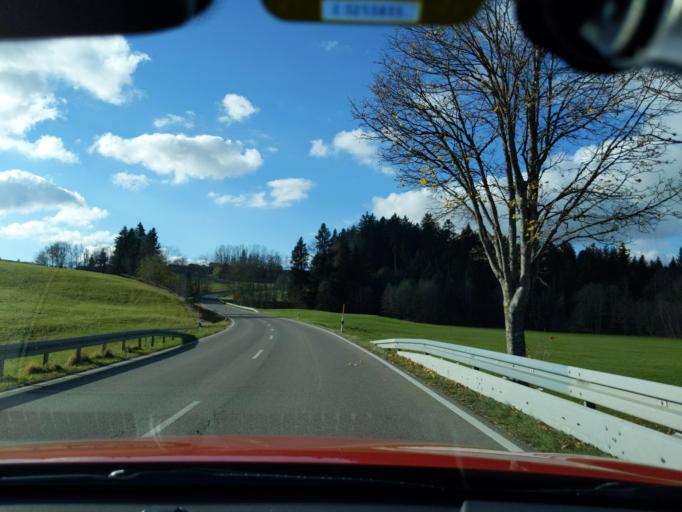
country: DE
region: Bavaria
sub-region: Swabia
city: Oberreute
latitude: 47.5656
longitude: 9.9575
